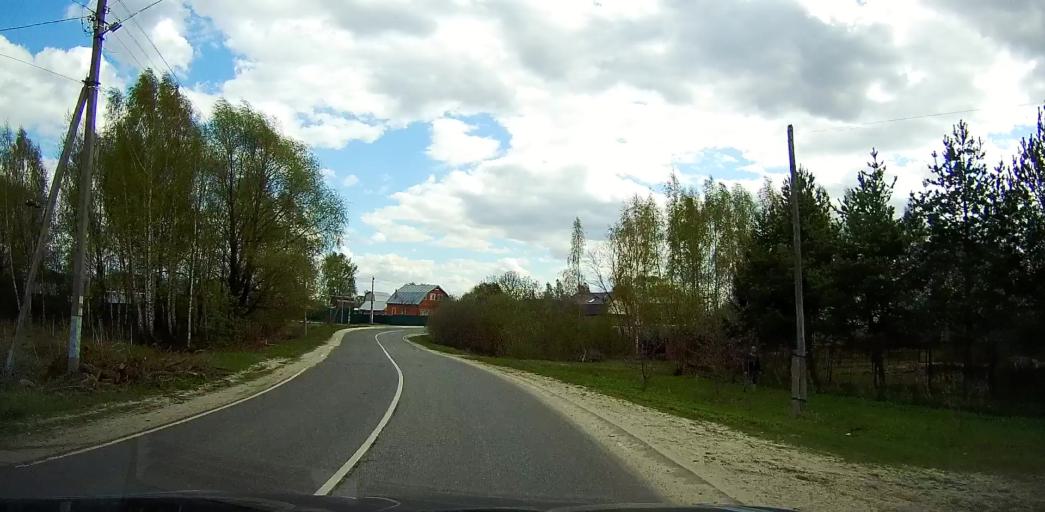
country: RU
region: Moskovskaya
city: Davydovo
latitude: 55.6460
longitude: 38.7502
